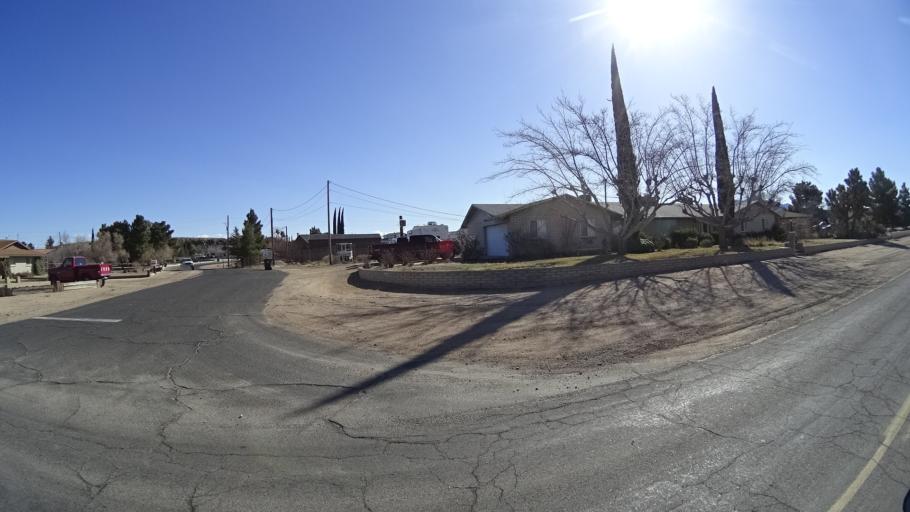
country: US
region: Arizona
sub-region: Mohave County
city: Kingman
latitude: 35.2041
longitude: -114.0114
